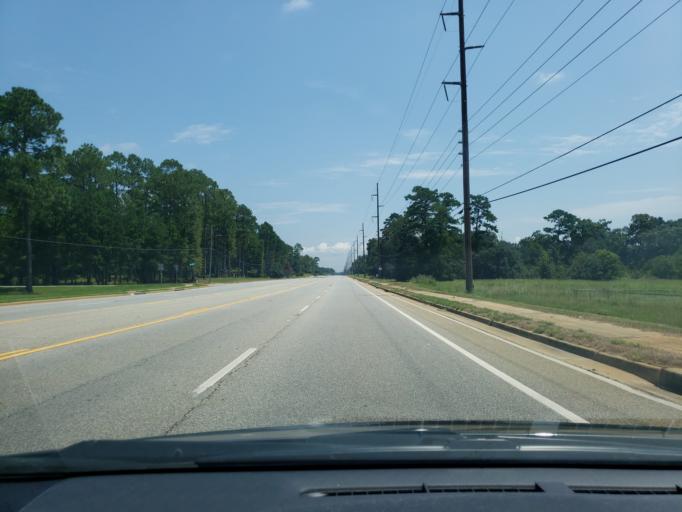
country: US
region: Georgia
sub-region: Dougherty County
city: Albany
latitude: 31.5856
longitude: -84.2485
